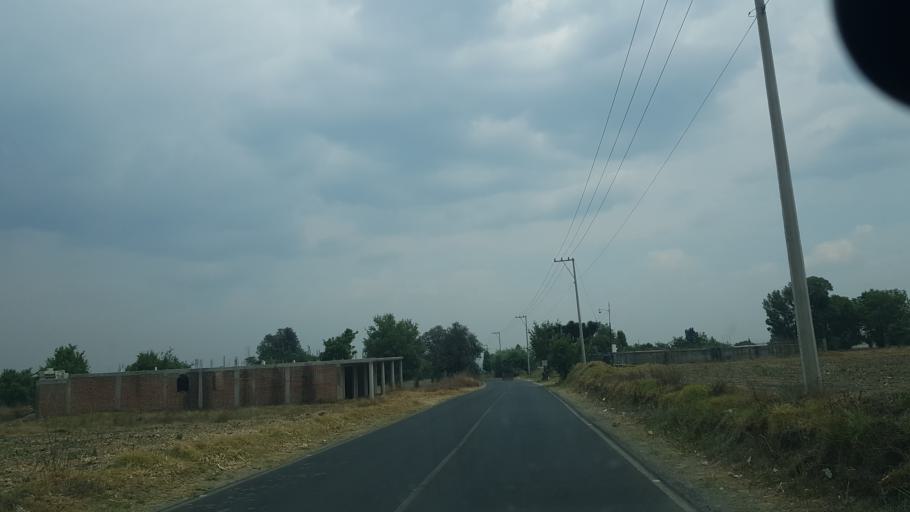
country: MX
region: Puebla
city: San Lorenzo Chiautzingo
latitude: 19.1983
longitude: -98.4518
